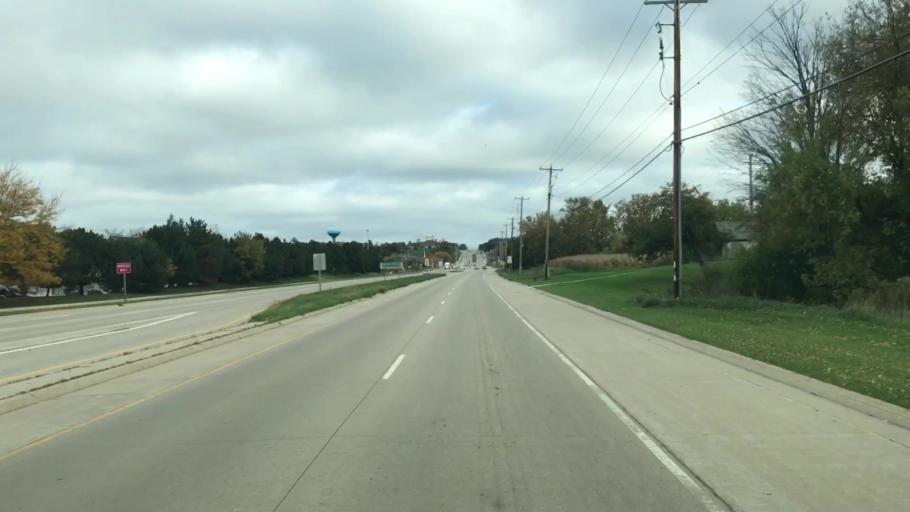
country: US
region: Wisconsin
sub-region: Waukesha County
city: Pewaukee
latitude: 43.0643
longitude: -88.2247
